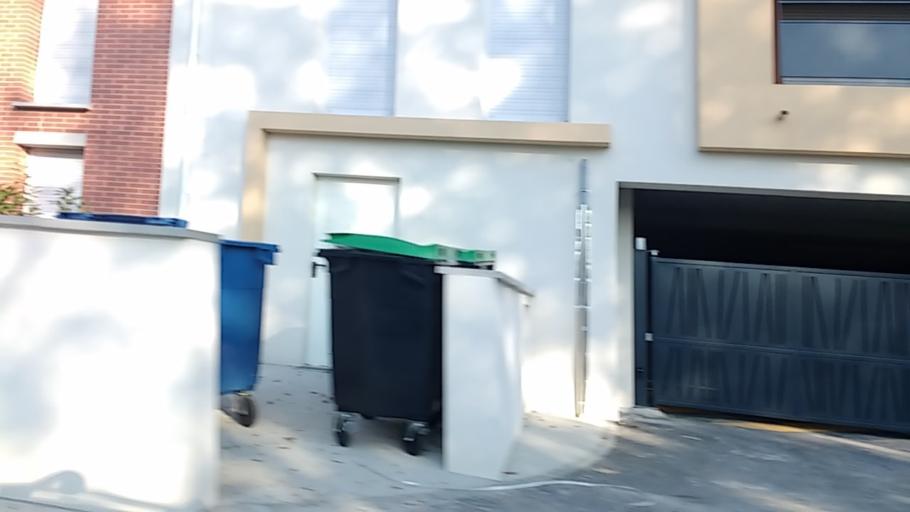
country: FR
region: Midi-Pyrenees
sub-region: Departement de la Haute-Garonne
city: Cugnaux
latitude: 43.5662
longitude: 1.3746
